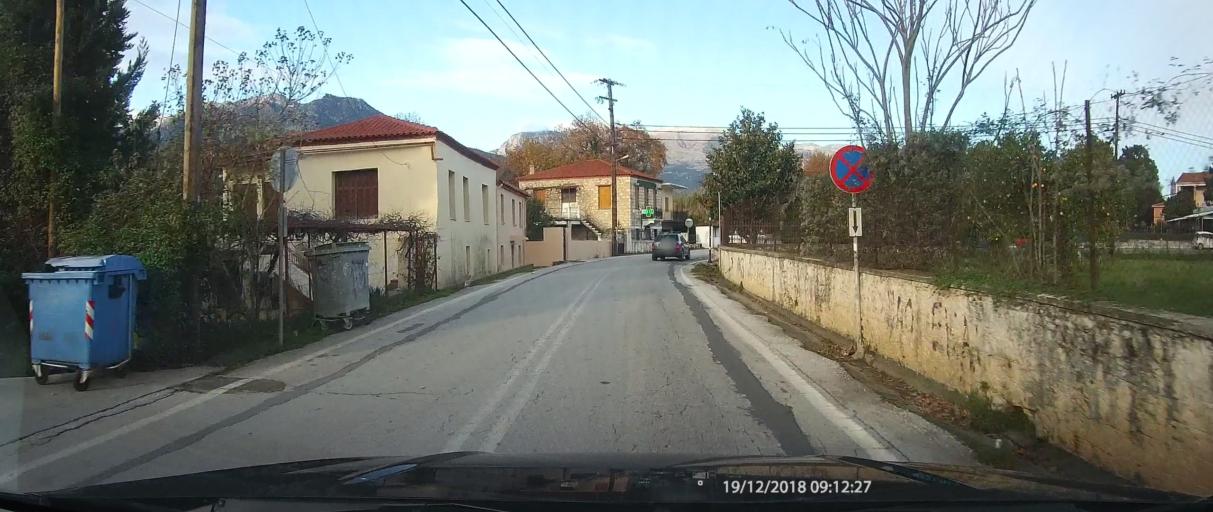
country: GR
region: Peloponnese
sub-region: Nomos Lakonias
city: Magoula
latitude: 37.0794
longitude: 22.4053
